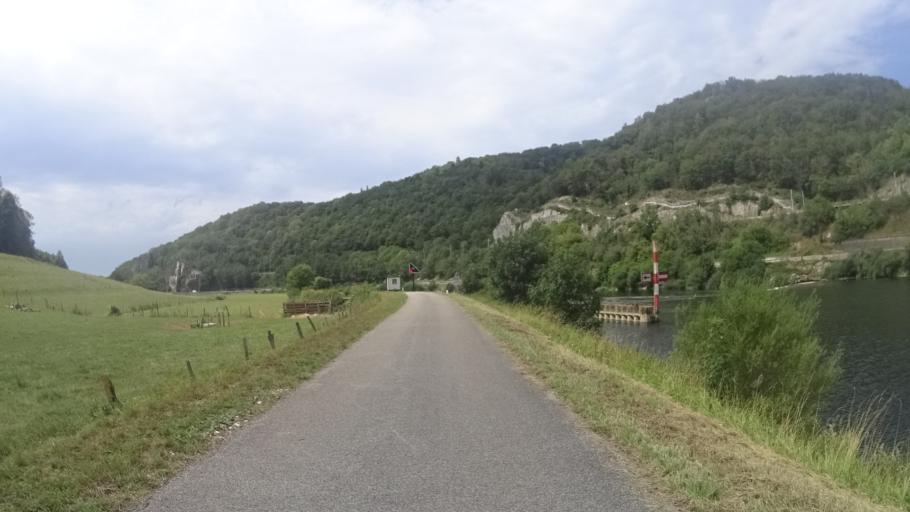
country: FR
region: Franche-Comte
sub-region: Departement du Doubs
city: Baume-les-Dames
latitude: 47.3573
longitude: 6.4006
